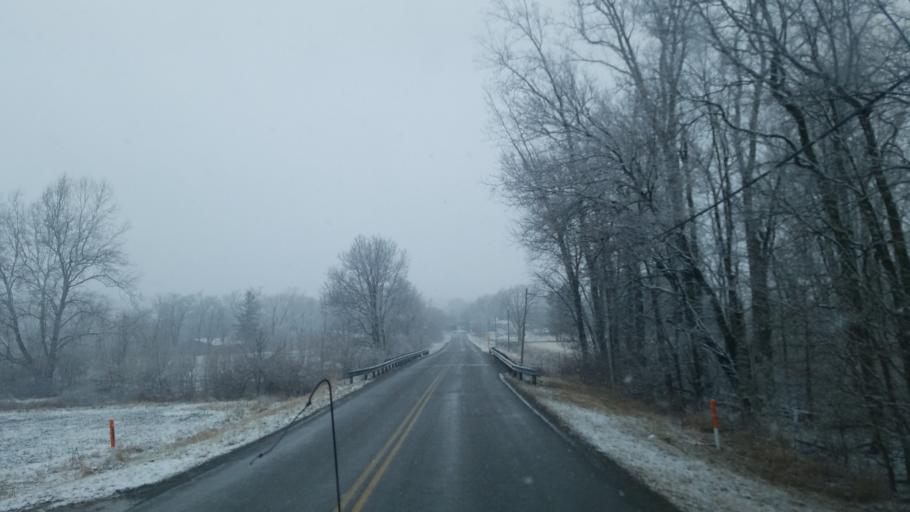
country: US
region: Ohio
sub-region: Logan County
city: Bellefontaine
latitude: 40.3351
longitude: -83.6731
